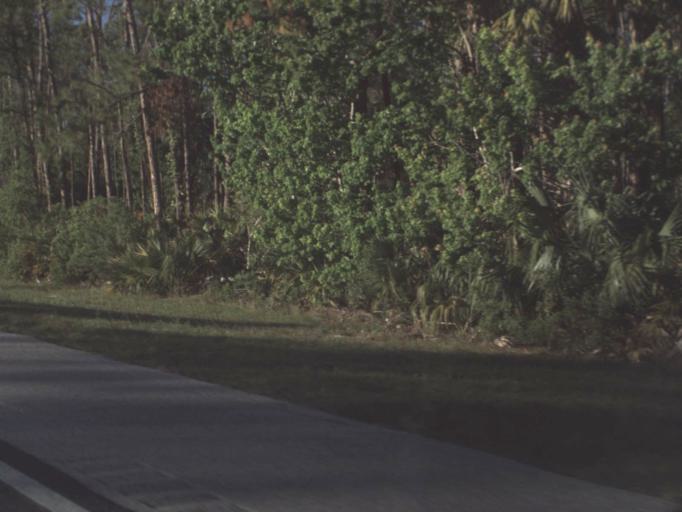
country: US
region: Florida
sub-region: Flagler County
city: Palm Coast
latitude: 29.6324
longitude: -81.2657
